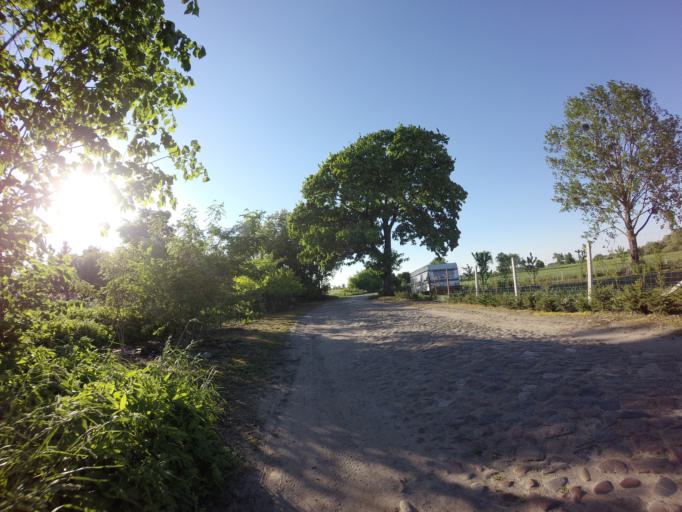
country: PL
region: West Pomeranian Voivodeship
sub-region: Powiat choszczenski
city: Choszczno
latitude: 53.1333
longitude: 15.4405
